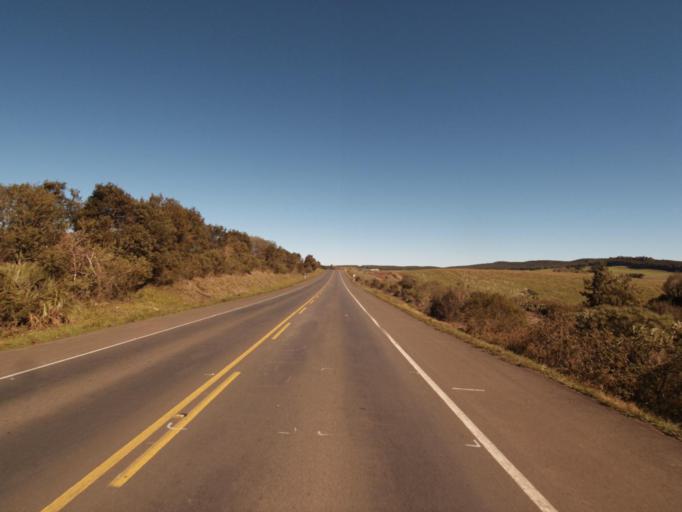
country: BR
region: Santa Catarina
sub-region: Concordia
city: Concordia
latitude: -26.9093
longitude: -51.9139
